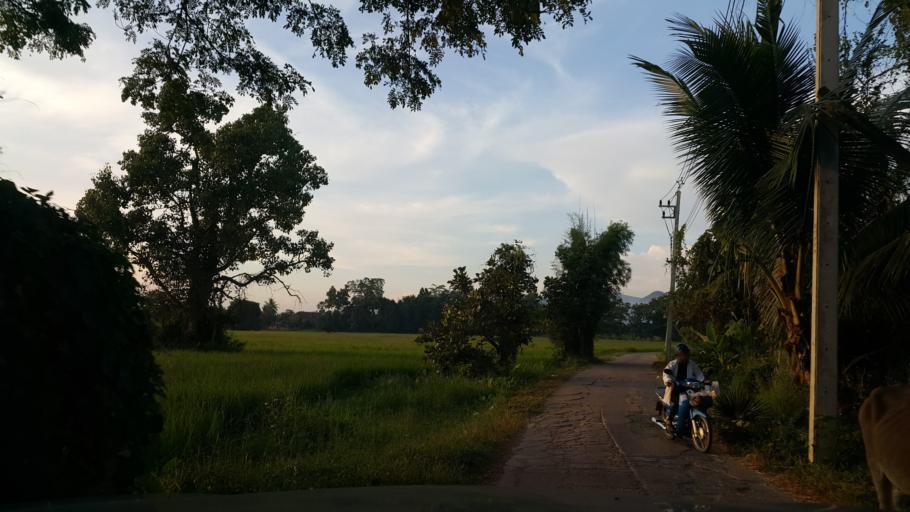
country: TH
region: Chiang Mai
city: San Sai
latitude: 18.8890
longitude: 99.0849
